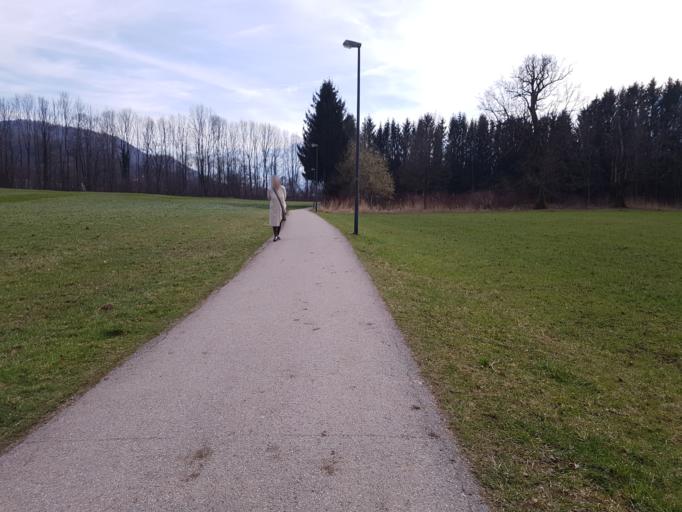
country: AT
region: Salzburg
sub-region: Politischer Bezirk Salzburg-Umgebung
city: Elsbethen
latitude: 47.7858
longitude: 13.0857
